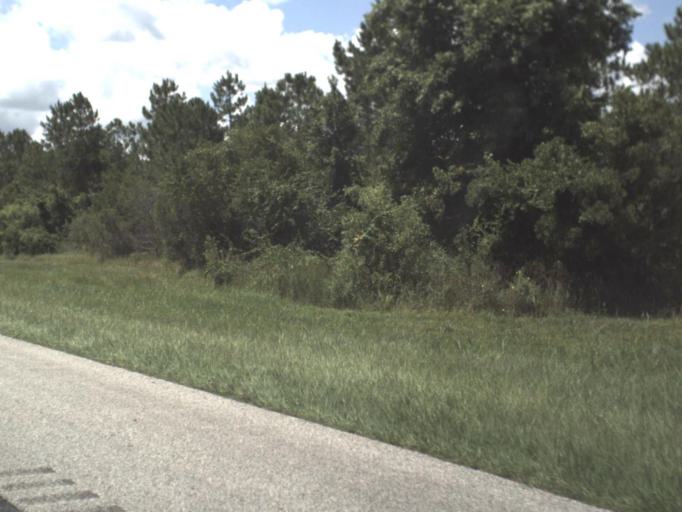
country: US
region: Florida
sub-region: Saint Johns County
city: Saint Augustine Shores
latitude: 29.7387
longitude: -81.3430
